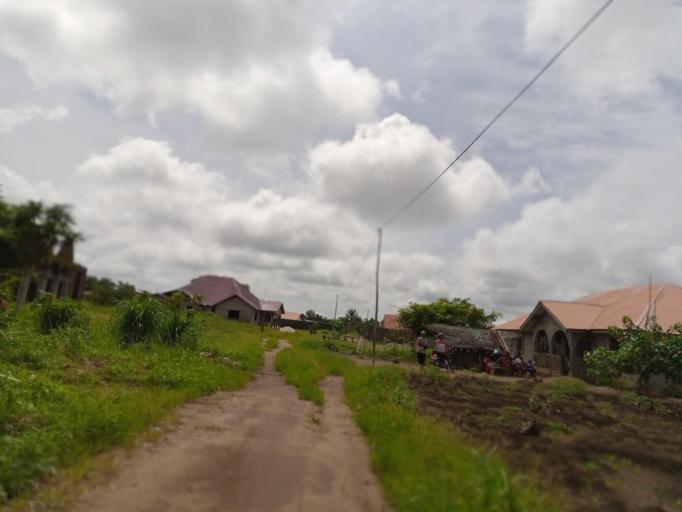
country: SL
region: Northern Province
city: Masoyila
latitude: 8.5919
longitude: -13.1954
